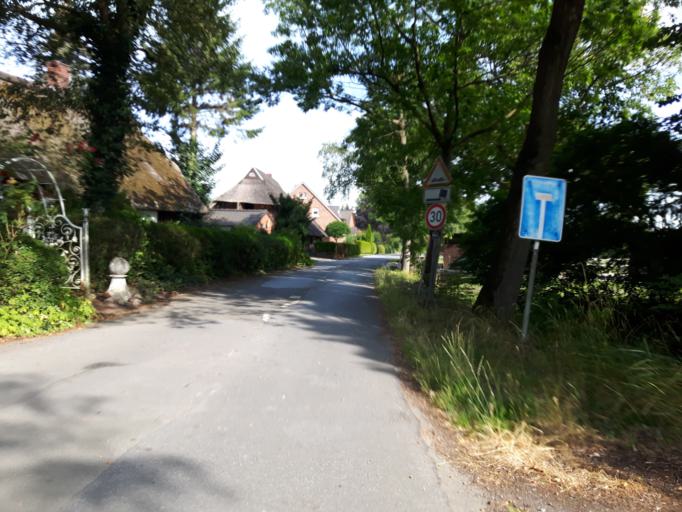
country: DE
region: Lower Saxony
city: Elsfleth
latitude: 53.2026
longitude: 8.4714
